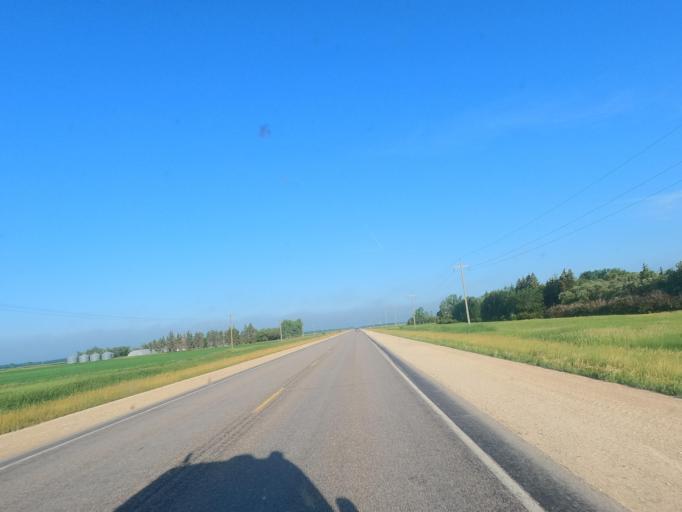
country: CA
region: Manitoba
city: Headingley
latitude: 49.7685
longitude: -97.5351
